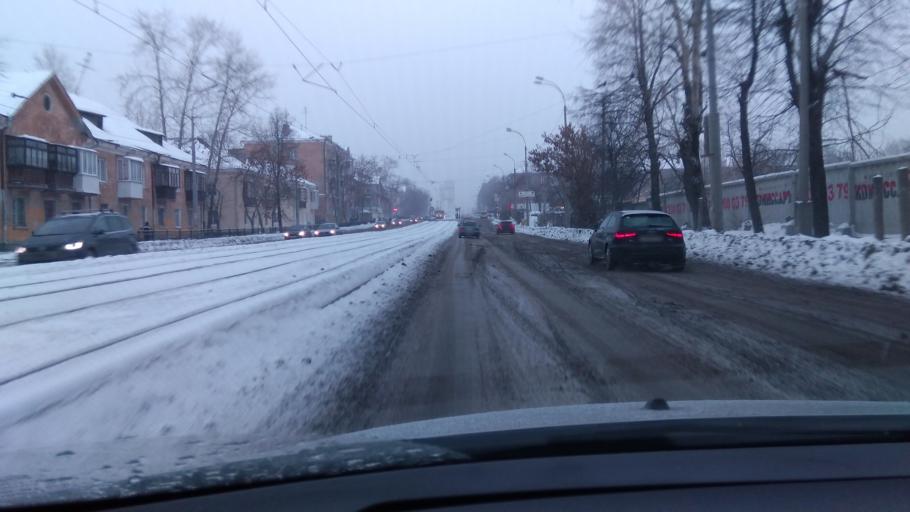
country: RU
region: Sverdlovsk
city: Yekaterinburg
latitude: 56.8995
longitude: 60.5802
